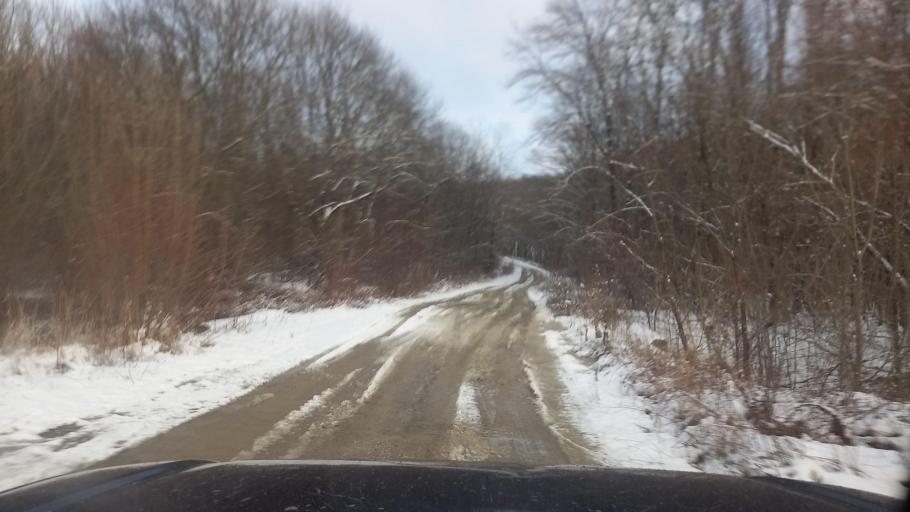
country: RU
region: Krasnodarskiy
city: Smolenskaya
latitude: 44.6749
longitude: 38.7609
